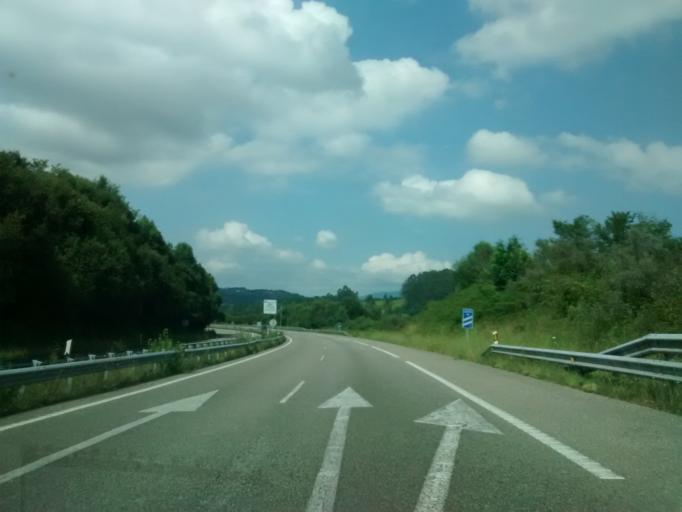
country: ES
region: Asturias
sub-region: Province of Asturias
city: Pola de Siero
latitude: 43.3485
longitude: -5.6826
